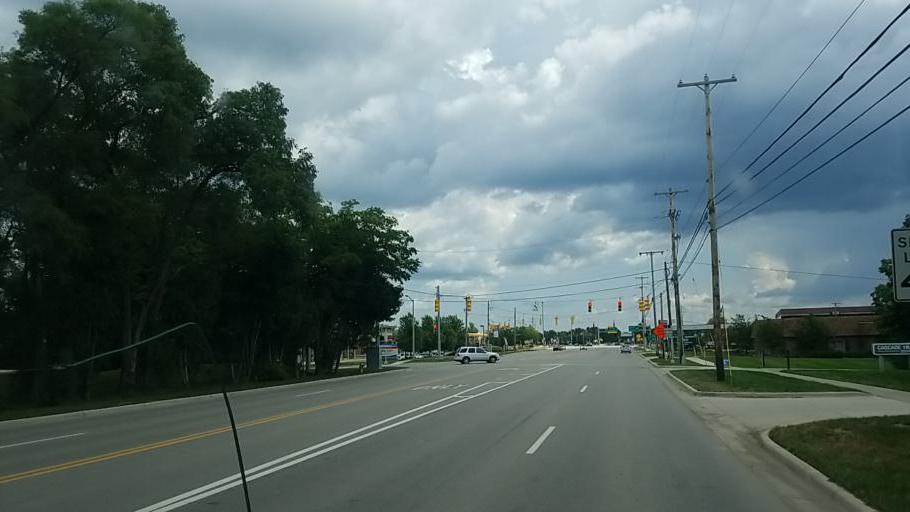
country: US
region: Michigan
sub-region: Kent County
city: East Grand Rapids
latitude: 42.9490
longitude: -85.5723
